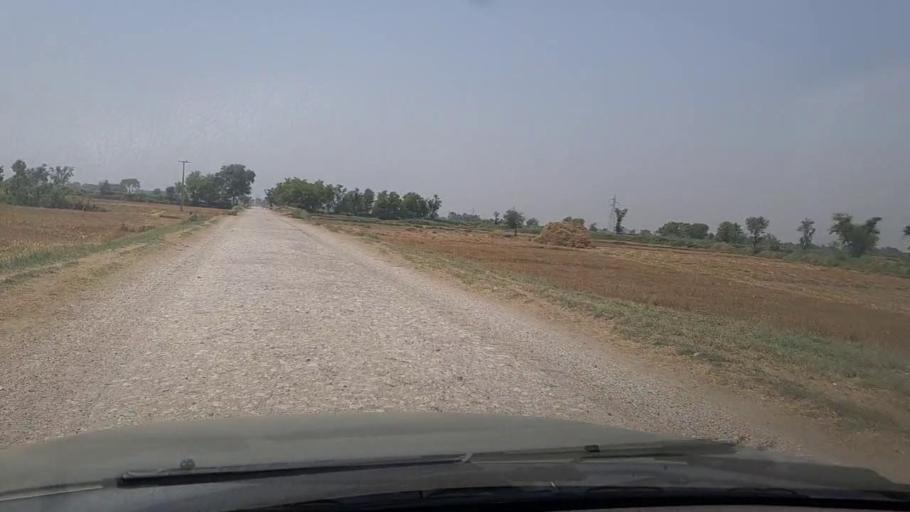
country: PK
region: Sindh
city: Miro Khan
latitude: 27.7776
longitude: 68.1779
